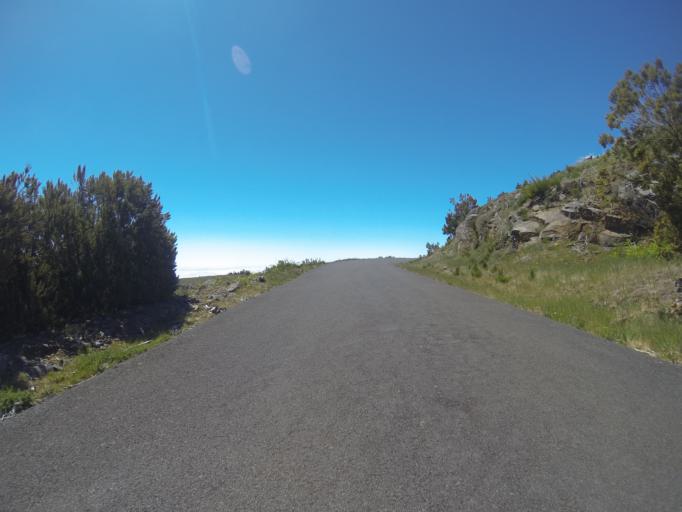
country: PT
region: Madeira
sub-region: Funchal
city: Nossa Senhora do Monte
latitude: 32.7187
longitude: -16.9117
